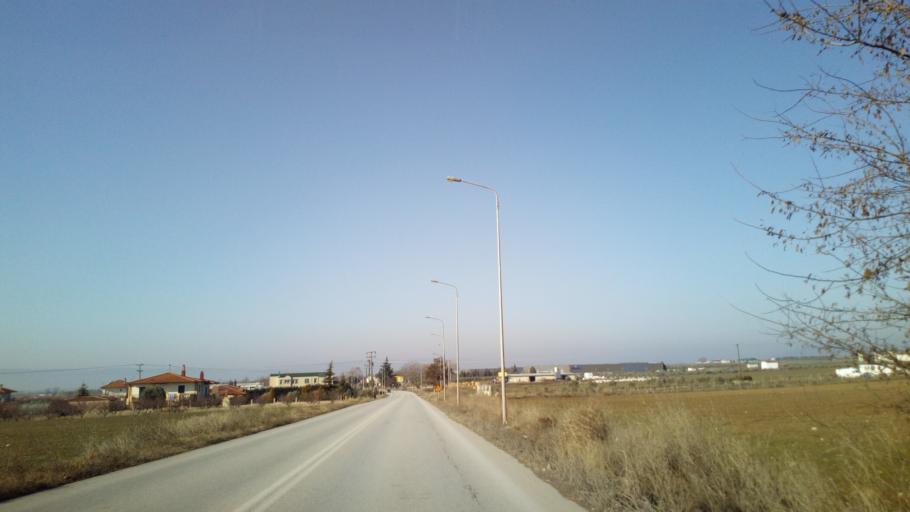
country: GR
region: Central Macedonia
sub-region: Nomos Thessalonikis
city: Kolchikon
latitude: 40.7552
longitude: 23.1236
